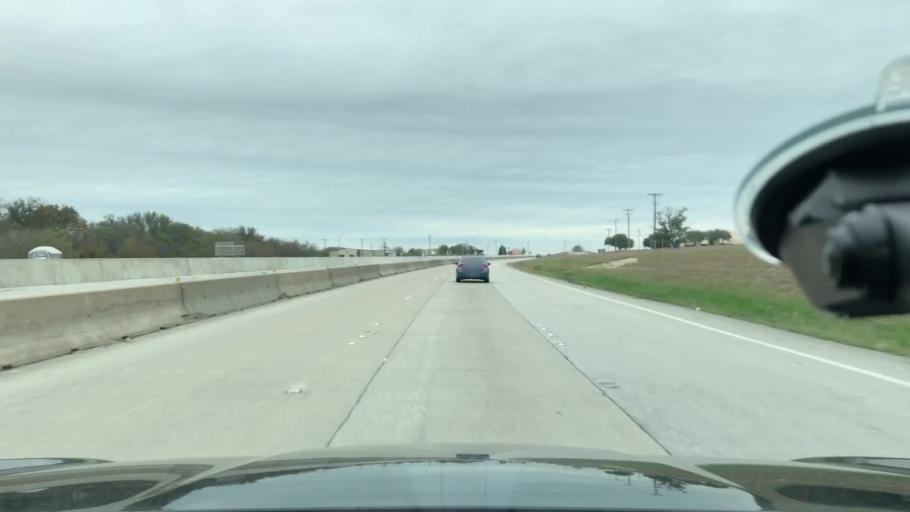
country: US
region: Texas
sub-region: Ellis County
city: Waxahachie
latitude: 32.4137
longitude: -96.8718
